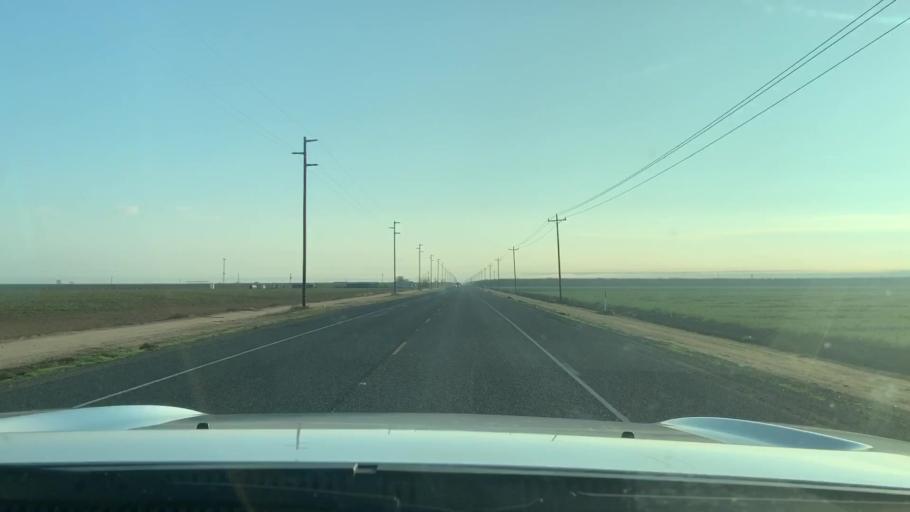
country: US
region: California
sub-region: Kern County
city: Wasco
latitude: 35.6010
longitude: -119.4885
